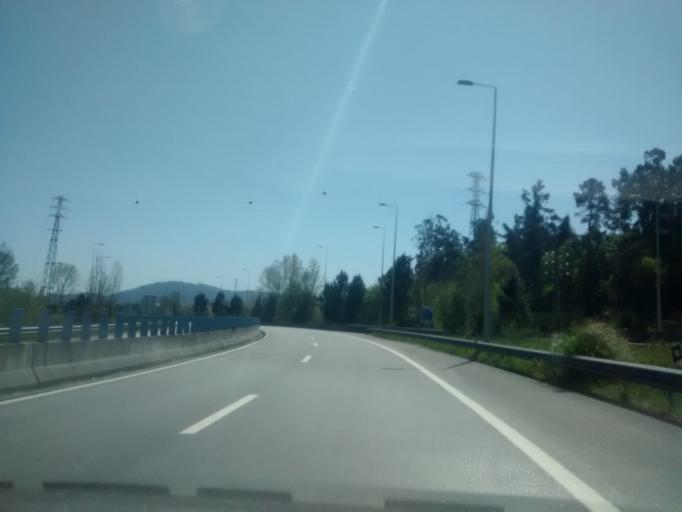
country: PT
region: Braga
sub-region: Braga
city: Oliveira
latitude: 41.5067
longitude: -8.4462
